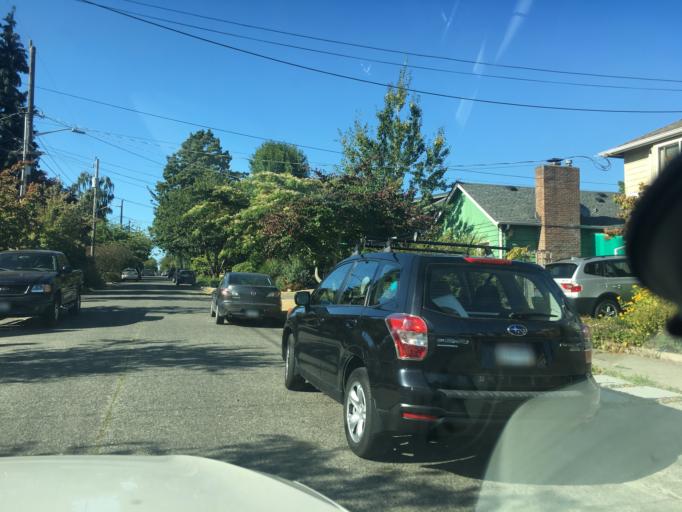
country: US
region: Washington
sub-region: King County
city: Shoreline
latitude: 47.6801
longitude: -122.3864
